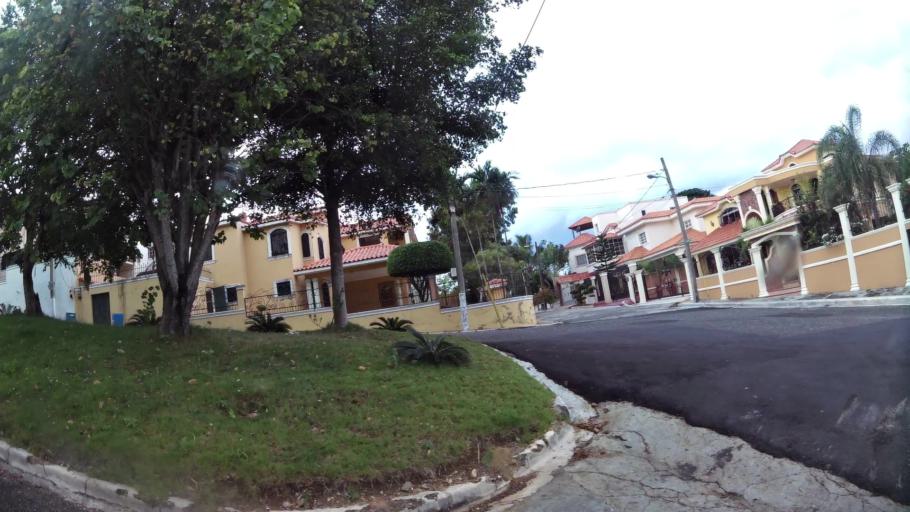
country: DO
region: Nacional
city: Santo Domingo
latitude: 18.4994
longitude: -69.9732
